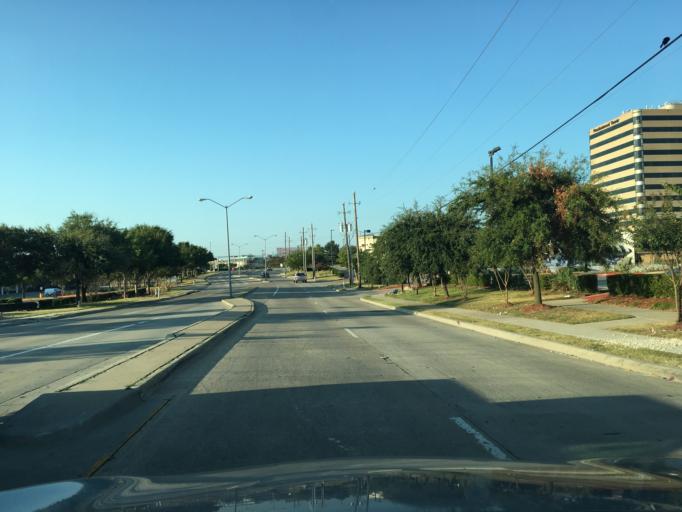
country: US
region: Texas
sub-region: Dallas County
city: Addison
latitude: 32.9564
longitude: -96.8185
